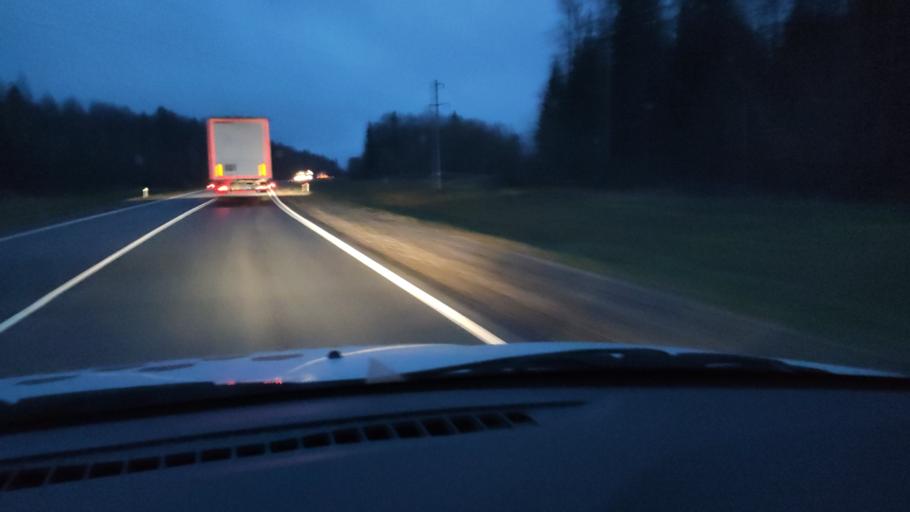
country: RU
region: Kirov
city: Kostino
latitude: 58.8159
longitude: 53.5824
